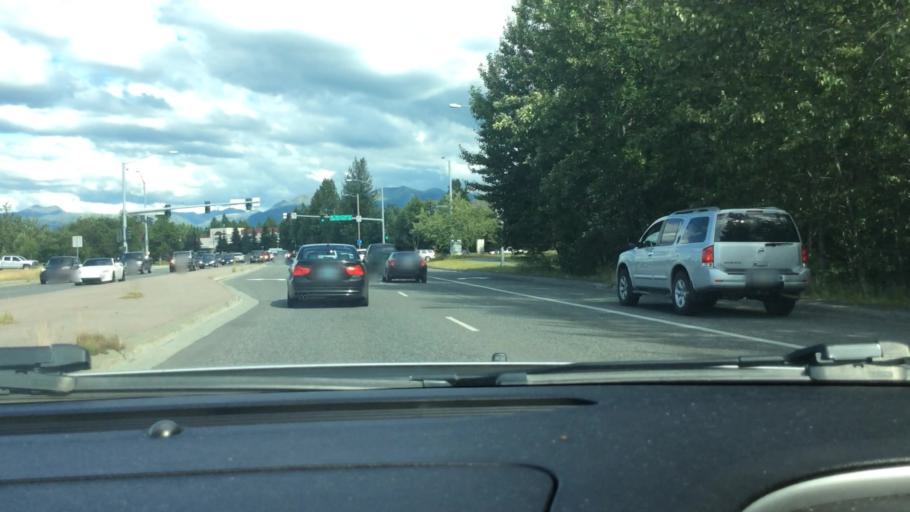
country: US
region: Alaska
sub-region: Anchorage Municipality
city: Anchorage
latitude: 61.2076
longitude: -149.8405
